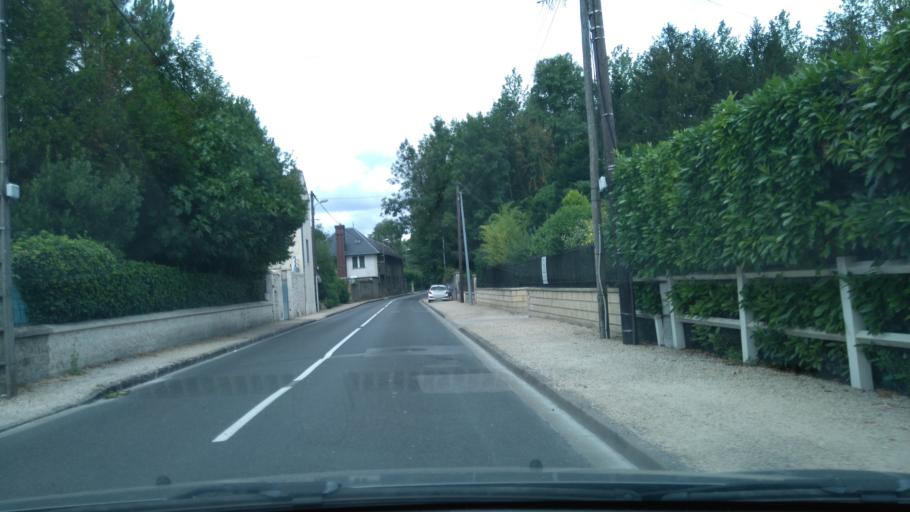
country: FR
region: Picardie
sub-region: Departement de l'Oise
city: Gouvieux
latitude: 49.1927
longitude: 2.4181
